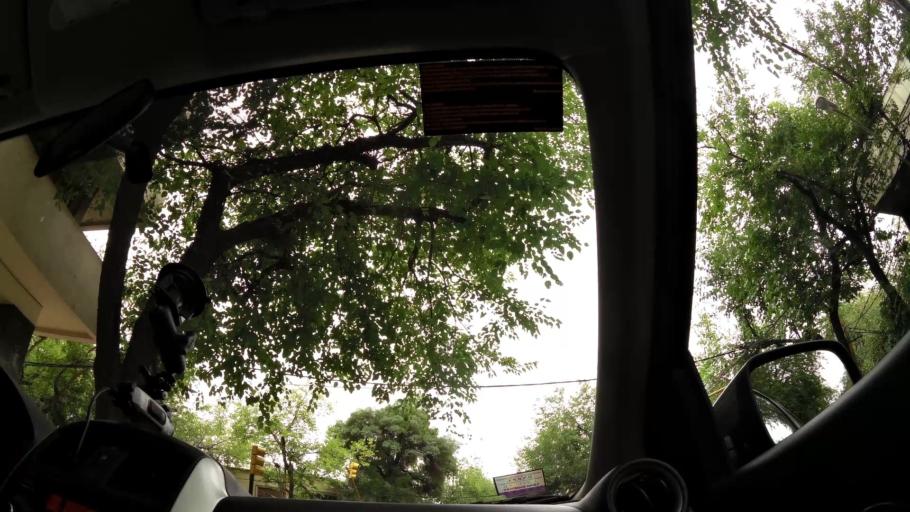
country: AR
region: Mendoza
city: Mendoza
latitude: -32.8892
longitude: -68.8484
